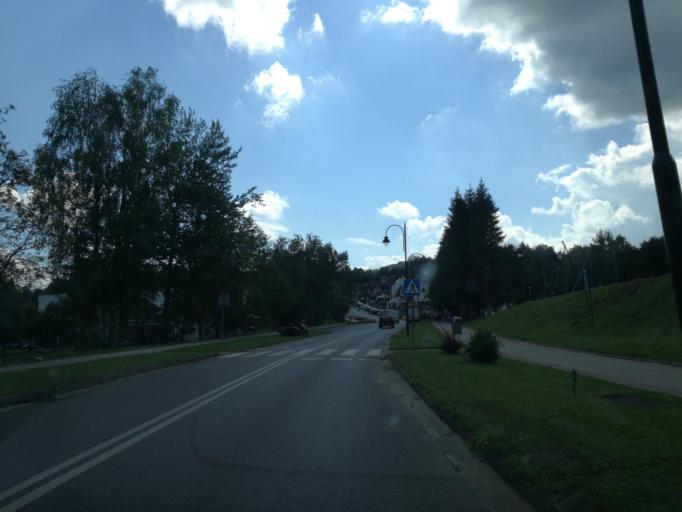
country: PL
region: Subcarpathian Voivodeship
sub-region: Powiat leski
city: Polanczyk
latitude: 49.3732
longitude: 22.4339
